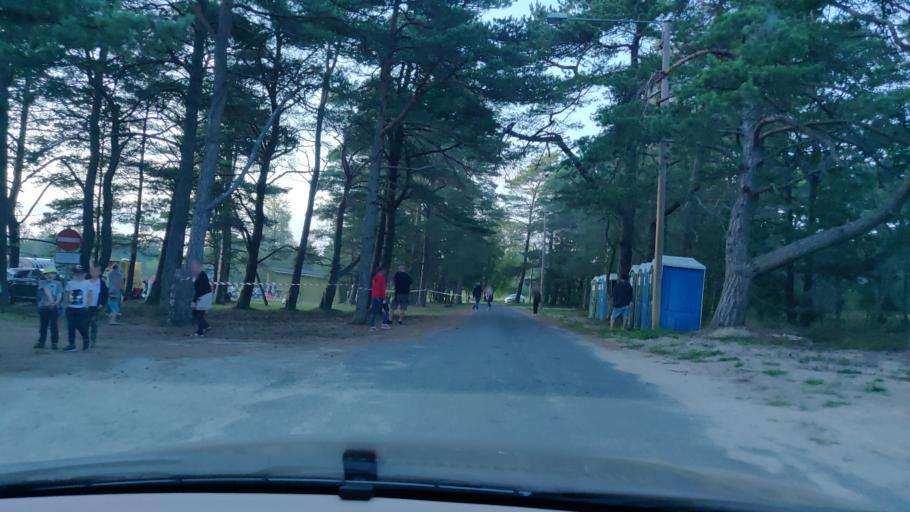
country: EE
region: Harju
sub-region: Keila linn
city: Keila
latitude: 59.3454
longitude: 24.2481
